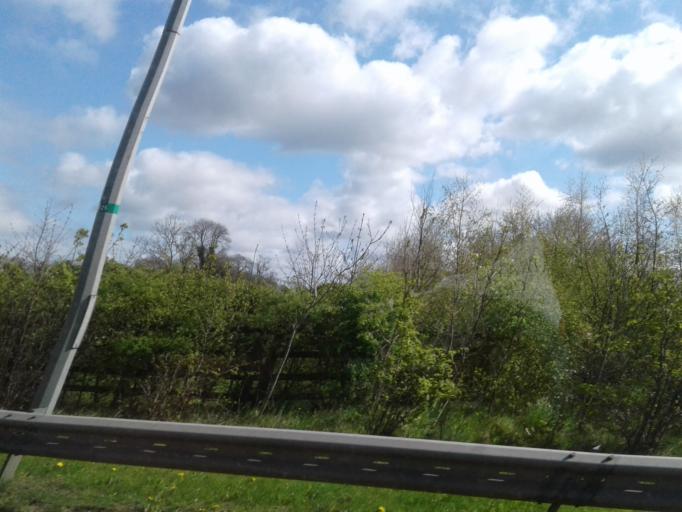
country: IE
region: Leinster
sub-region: An Mhi
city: Ashbourne
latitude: 53.4914
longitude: -6.3869
